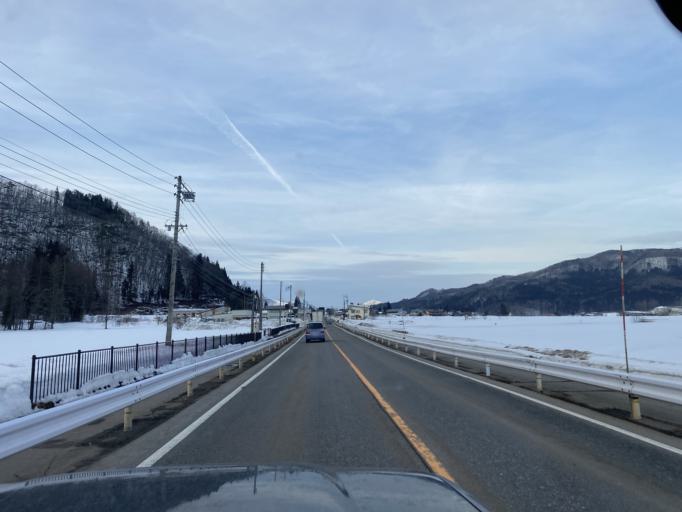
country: JP
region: Nagano
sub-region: Kitaazumi Gun
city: Hakuba
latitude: 36.6488
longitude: 137.8453
